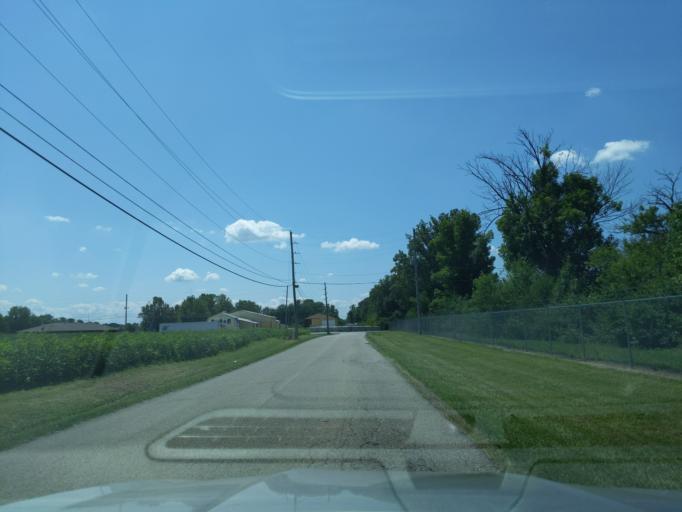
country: US
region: Indiana
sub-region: Decatur County
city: Greensburg
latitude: 39.3578
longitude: -85.4891
